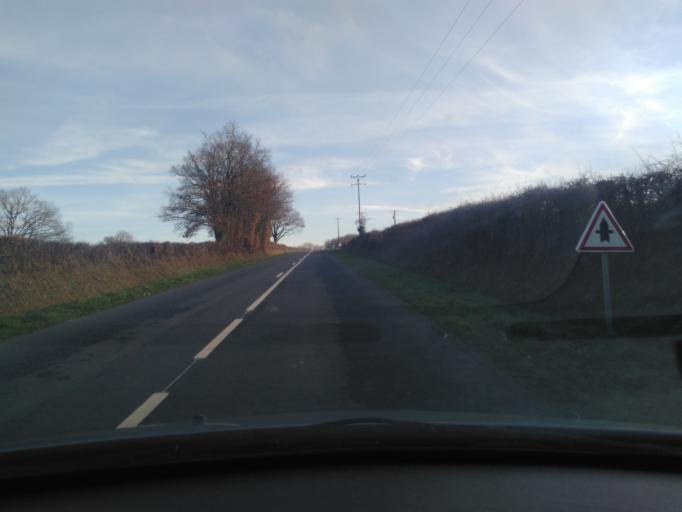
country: FR
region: Centre
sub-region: Departement de l'Indre
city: Montgivray
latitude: 46.6396
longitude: 2.0940
